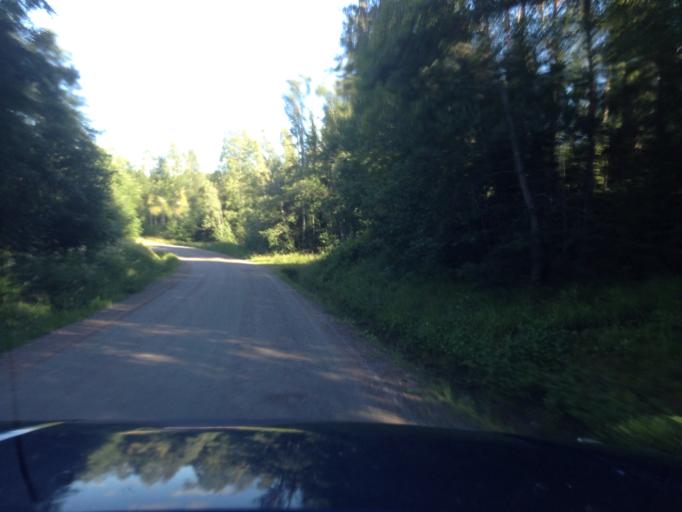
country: SE
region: Dalarna
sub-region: Ludvika Kommun
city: Abborrberget
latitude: 60.2329
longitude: 14.8239
